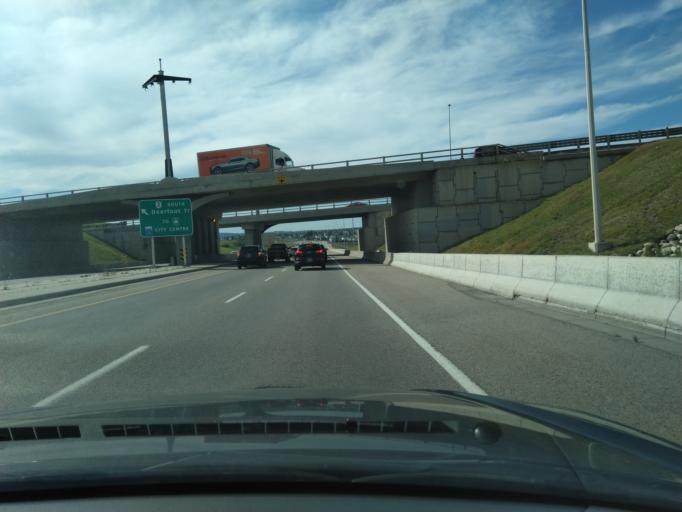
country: CA
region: Alberta
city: Calgary
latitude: 51.1411
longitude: -114.0340
